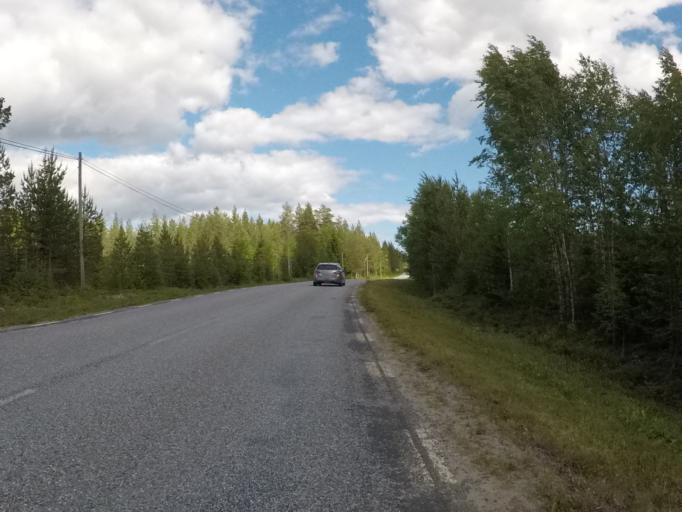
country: SE
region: Vaesterbotten
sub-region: Robertsfors Kommun
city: Robertsfors
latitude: 63.9537
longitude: 20.7953
